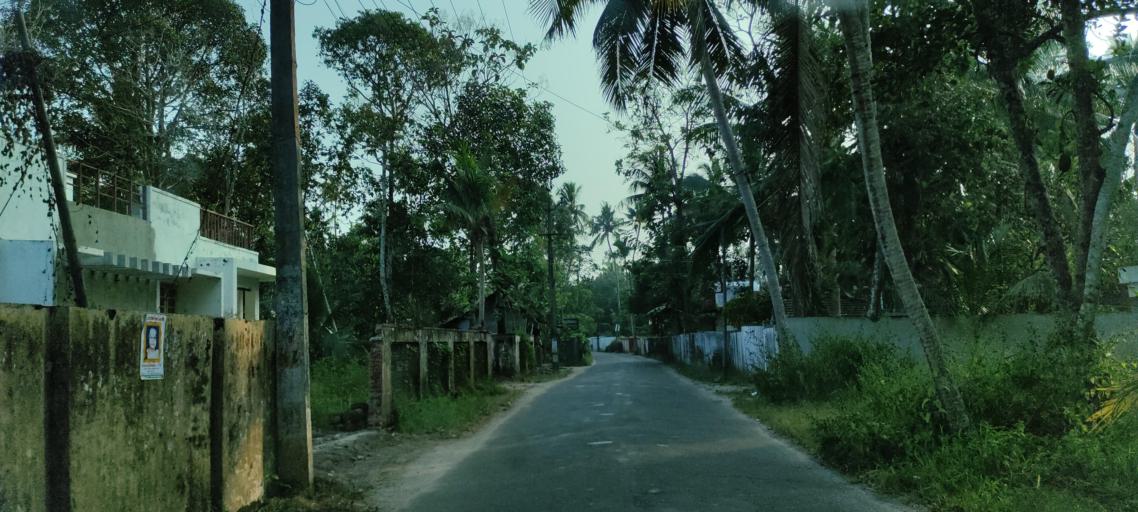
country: IN
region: Kerala
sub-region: Alappuzha
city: Shertallai
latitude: 9.6677
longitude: 76.3537
